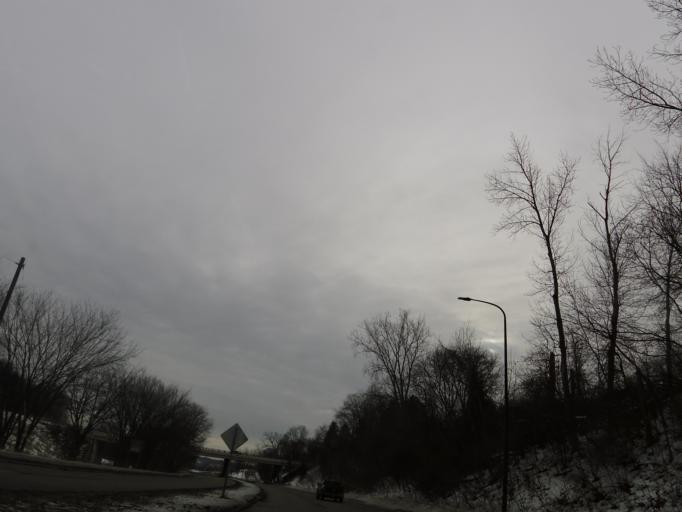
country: US
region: Minnesota
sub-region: Dakota County
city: West Saint Paul
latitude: 44.9327
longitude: -93.1486
